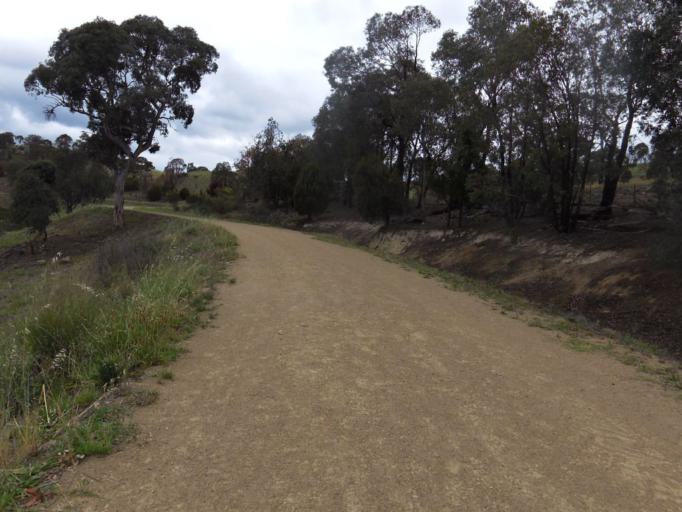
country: AU
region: Australian Capital Territory
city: Macquarie
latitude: -35.3526
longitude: 149.0257
